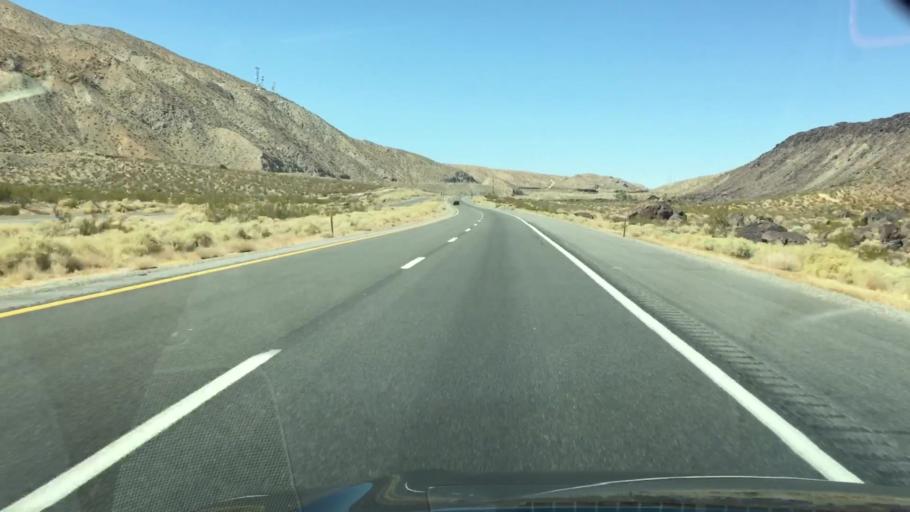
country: US
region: California
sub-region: Kern County
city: Inyokern
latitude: 35.9128
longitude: -117.9038
